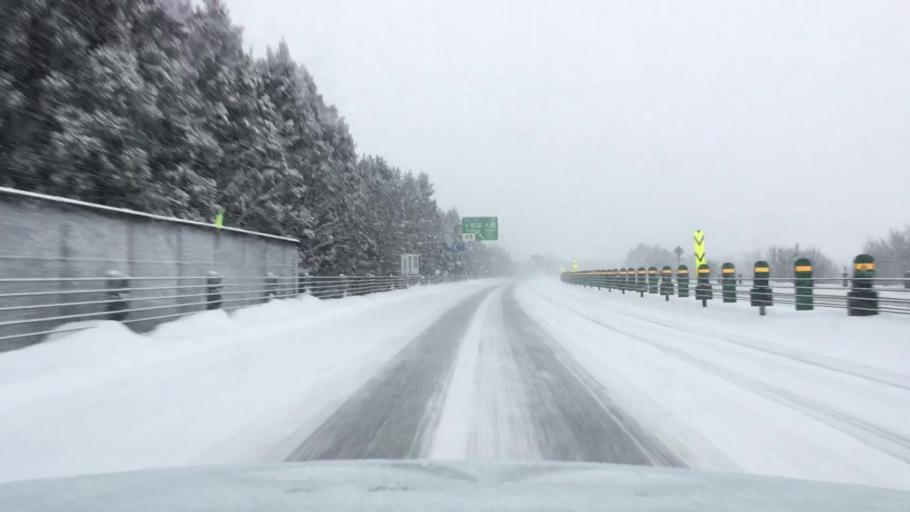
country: JP
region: Akita
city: Hanawa
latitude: 40.2514
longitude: 140.7663
